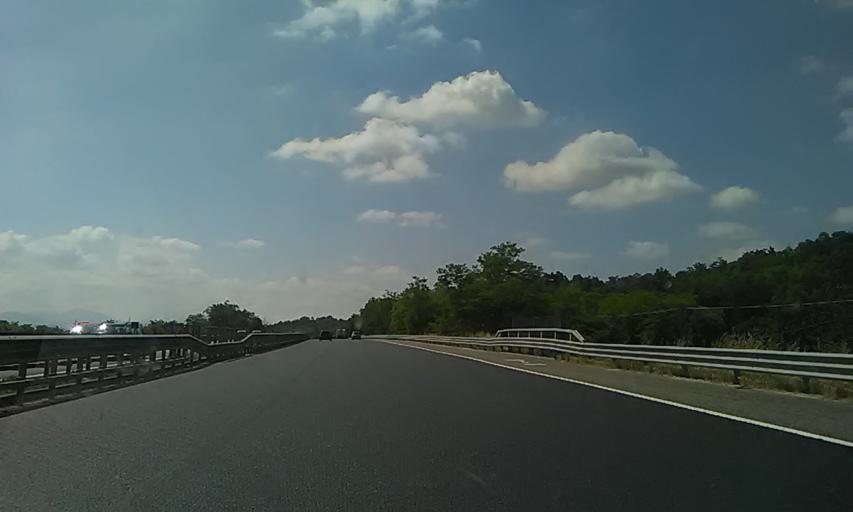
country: IT
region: Piedmont
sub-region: Provincia di Alessandria
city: Predosa
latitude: 44.7477
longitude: 8.6475
